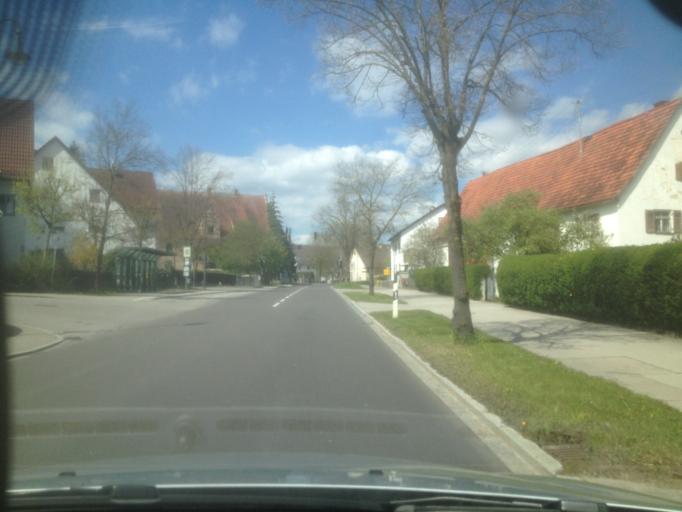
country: DE
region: Bavaria
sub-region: Swabia
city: Diedorf
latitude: 48.3745
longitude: 10.7645
